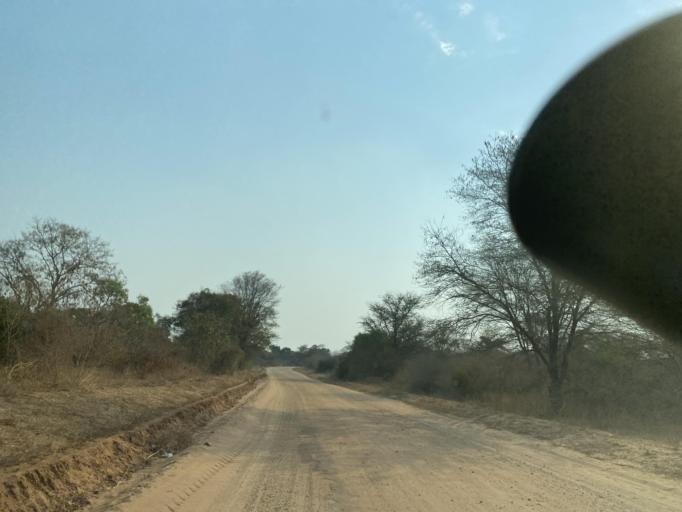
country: ZW
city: Chirundu
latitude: -15.9354
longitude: 28.9351
